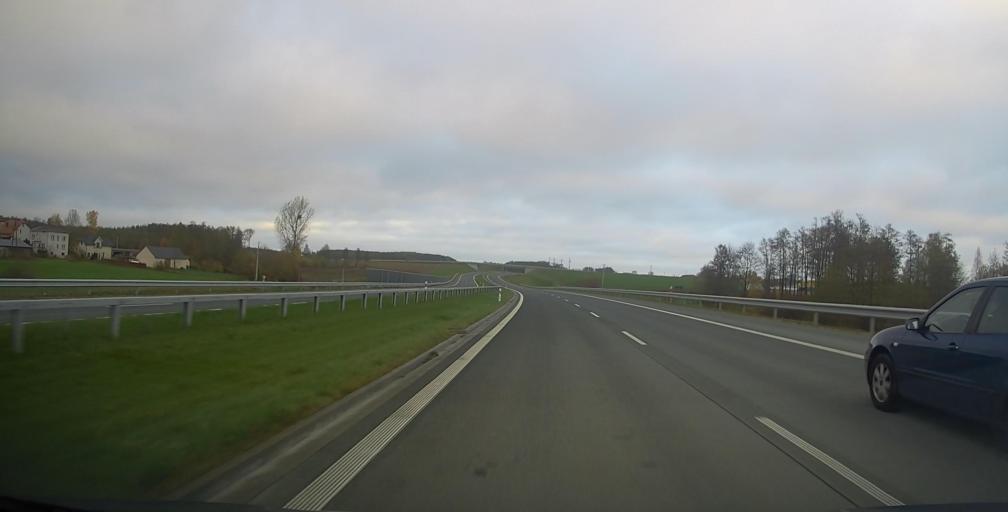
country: PL
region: Podlasie
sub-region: Powiat grajewski
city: Szczuczyn
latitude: 53.5252
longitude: 22.2607
